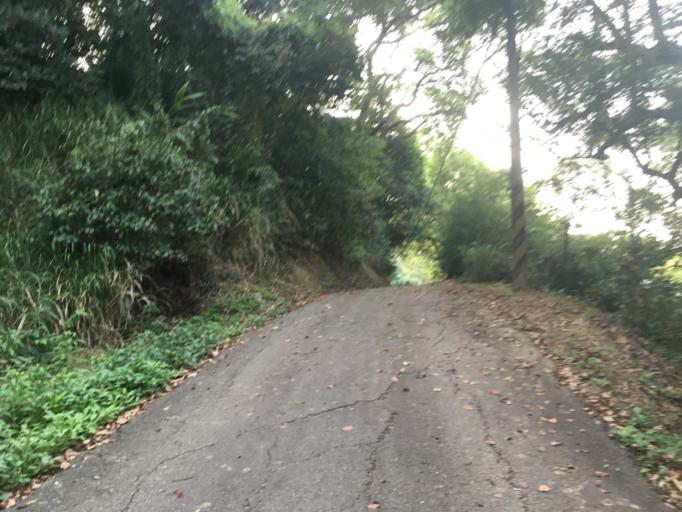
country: TW
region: Taiwan
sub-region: Hsinchu
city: Hsinchu
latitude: 24.7601
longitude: 120.9756
